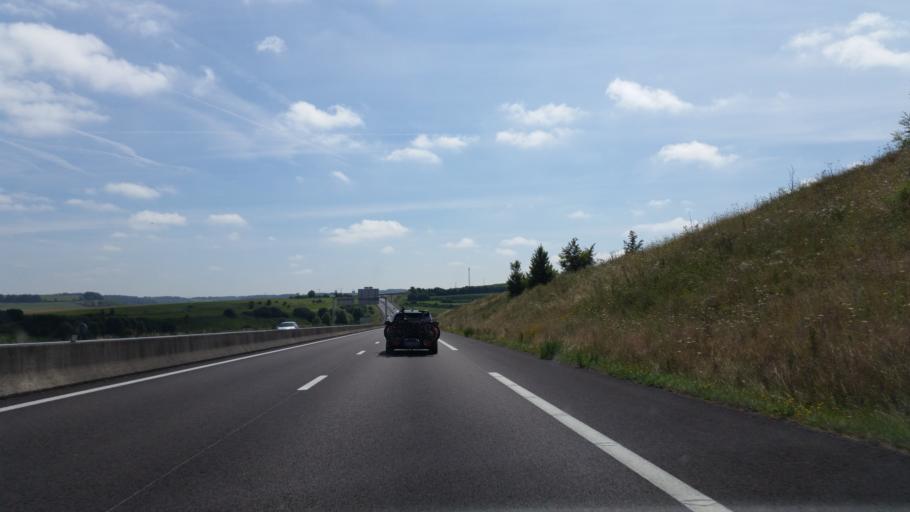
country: FR
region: Haute-Normandie
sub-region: Departement de la Seine-Maritime
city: Neufchatel-en-Bray
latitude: 49.7438
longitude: 1.5306
